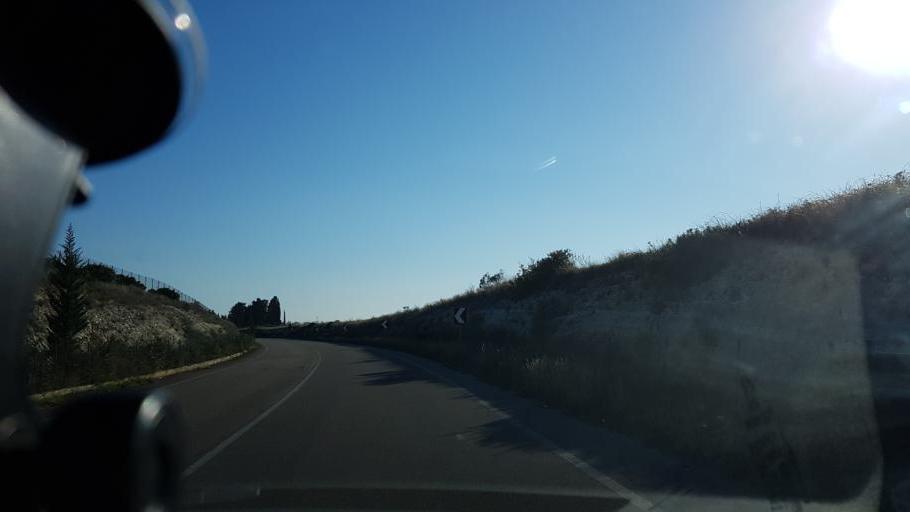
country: IT
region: Apulia
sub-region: Provincia di Lecce
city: Merine
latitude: 40.4052
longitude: 18.2505
